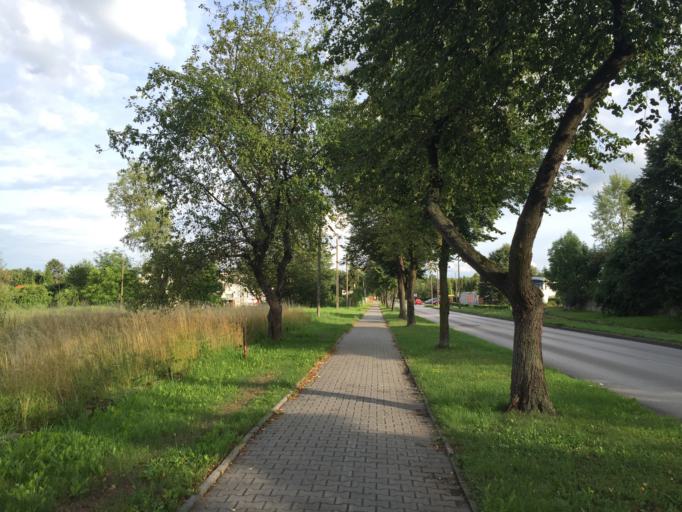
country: PL
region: Lesser Poland Voivodeship
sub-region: Powiat oswiecimski
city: Brzezinka
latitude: 50.0338
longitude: 19.1969
